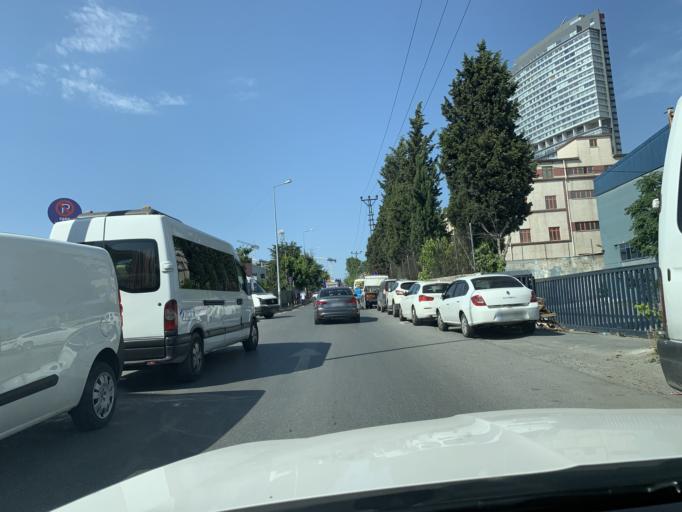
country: TR
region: Istanbul
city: Esenyurt
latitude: 41.0611
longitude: 28.6627
